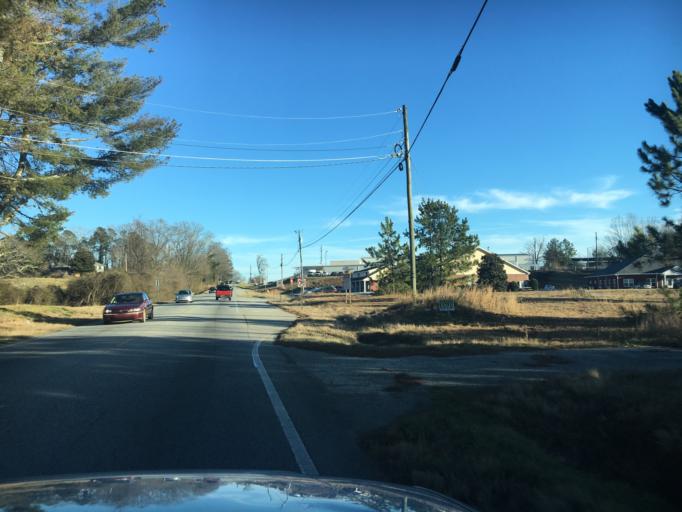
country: US
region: Georgia
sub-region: Habersham County
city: Demorest
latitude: 34.5473
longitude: -83.5522
